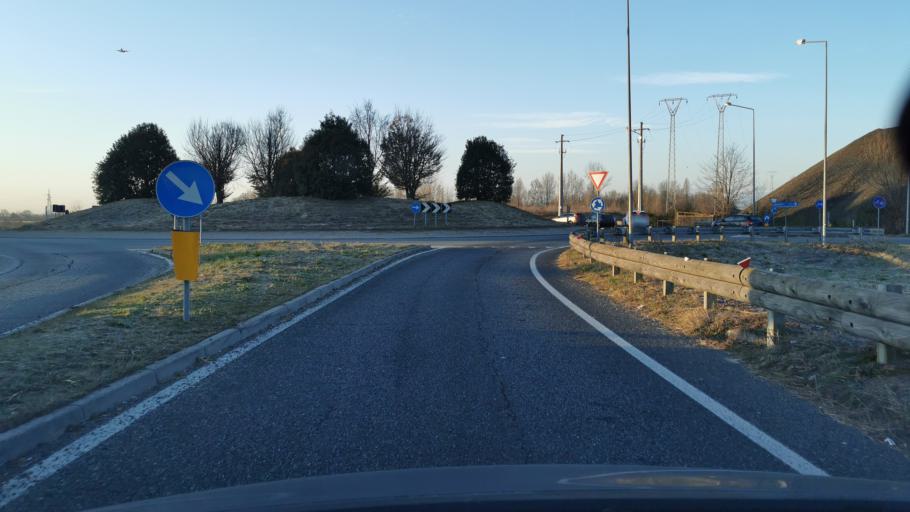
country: IT
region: Piedmont
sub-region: Provincia di Torino
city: Borgaro Torinese
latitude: 45.1542
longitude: 7.6444
